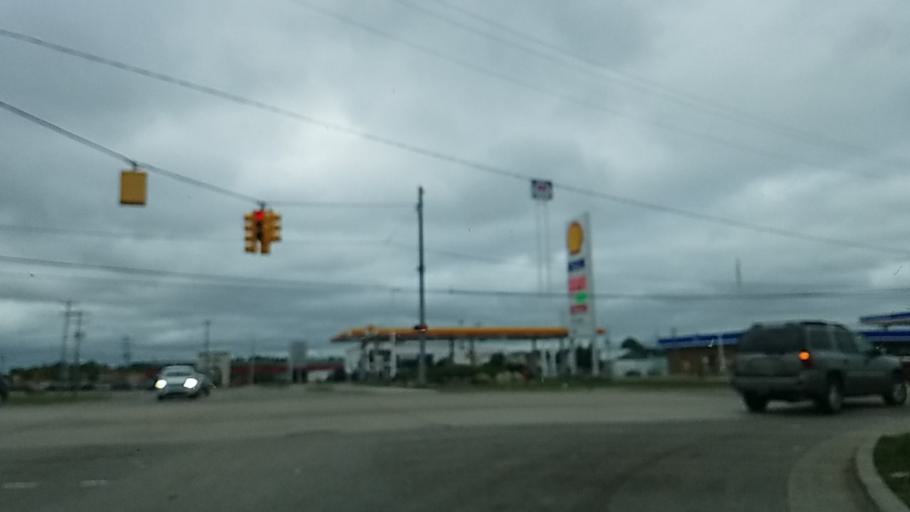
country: US
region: Michigan
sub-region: Otsego County
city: Gaylord
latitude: 45.0276
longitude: -84.6911
